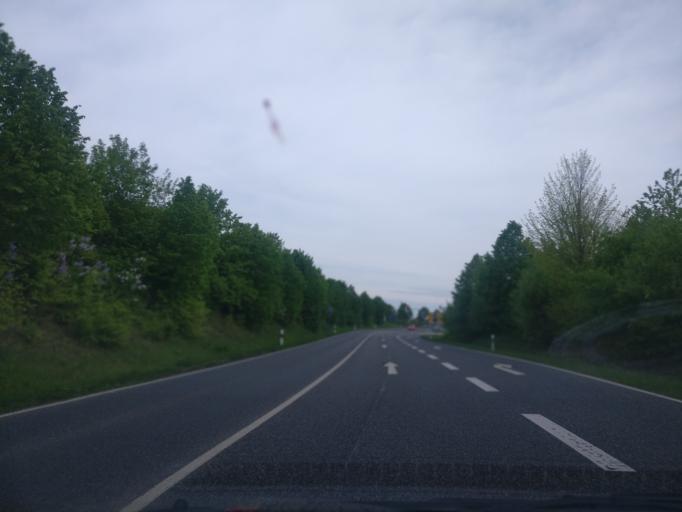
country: DE
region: Hesse
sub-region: Regierungsbezirk Kassel
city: Vellmar
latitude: 51.3541
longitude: 9.5153
